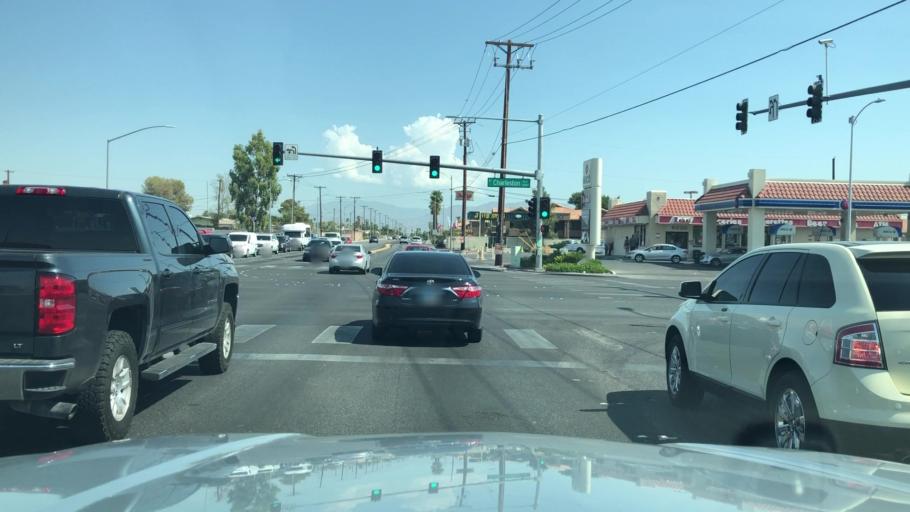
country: US
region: Nevada
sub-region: Clark County
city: Spring Valley
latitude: 36.1590
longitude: -115.2238
